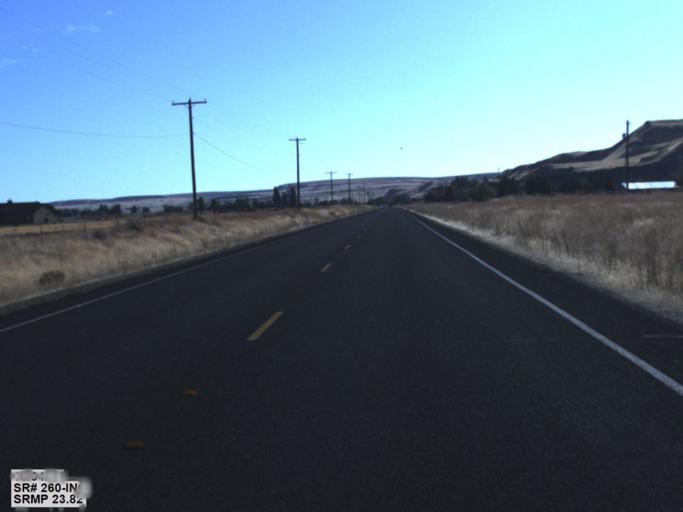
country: US
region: Washington
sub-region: Franklin County
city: Connell
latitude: 46.6454
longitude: -118.5766
